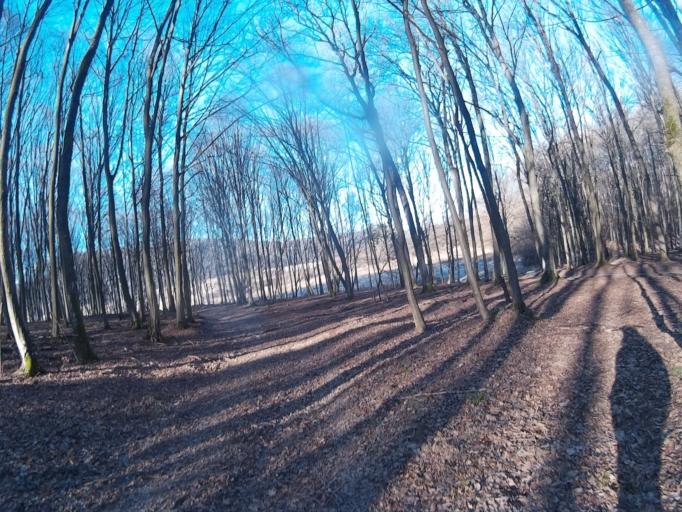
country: HU
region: Borsod-Abauj-Zemplen
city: Rudabanya
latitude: 48.5117
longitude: 20.6062
